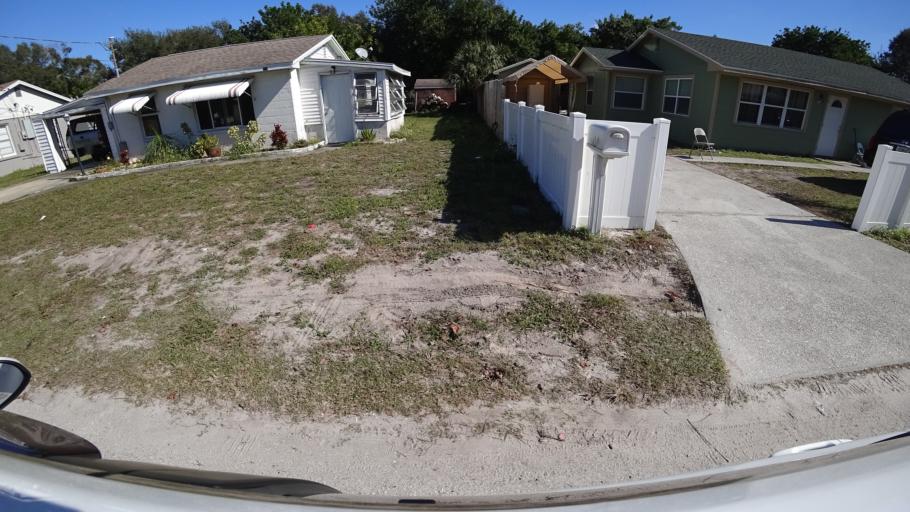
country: US
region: Florida
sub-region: Manatee County
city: West Samoset
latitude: 27.4800
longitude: -82.5605
